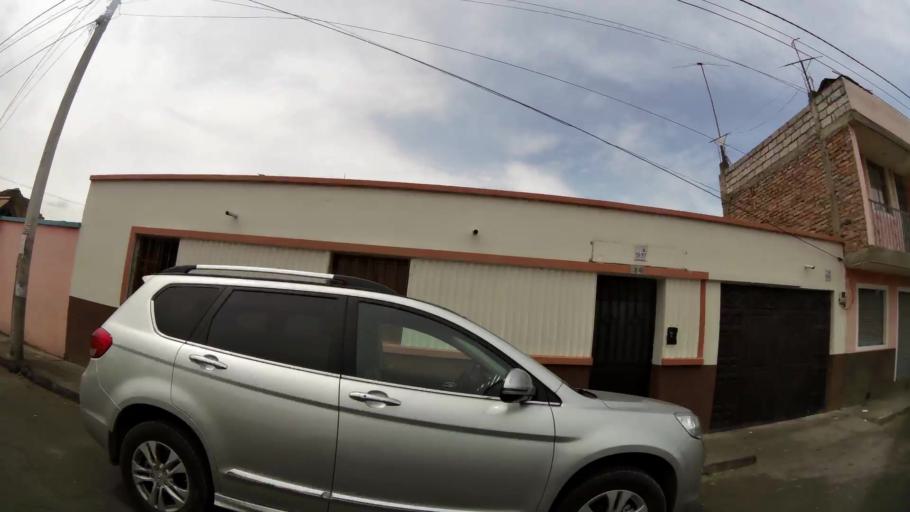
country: EC
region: Cotopaxi
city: Latacunga
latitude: -0.9288
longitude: -78.6124
